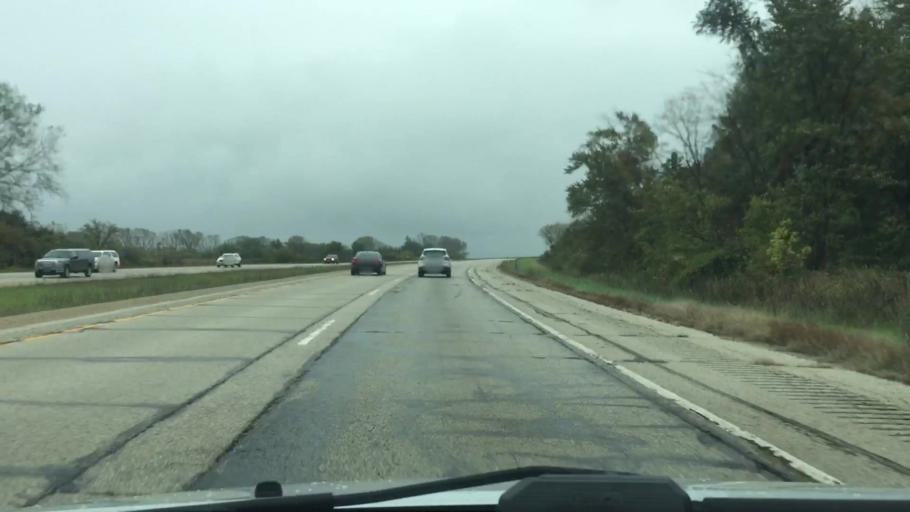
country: US
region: Wisconsin
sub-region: Walworth County
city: Como
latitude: 42.6336
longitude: -88.4761
